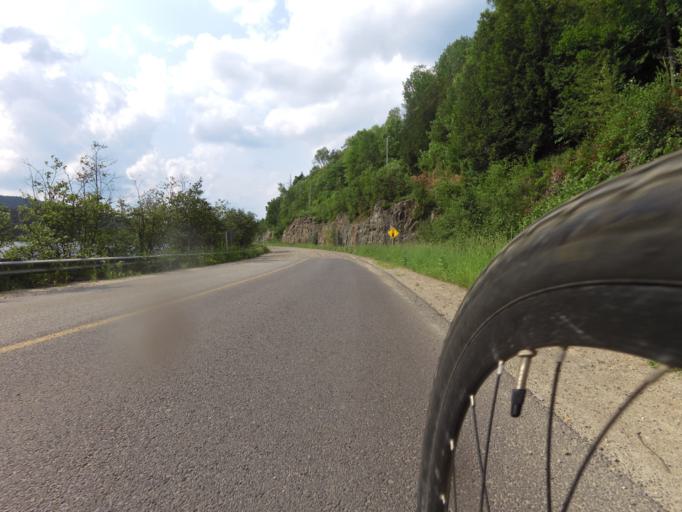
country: CA
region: Quebec
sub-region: Laurentides
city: Brownsburg-Chatham
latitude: 45.9134
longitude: -74.5974
